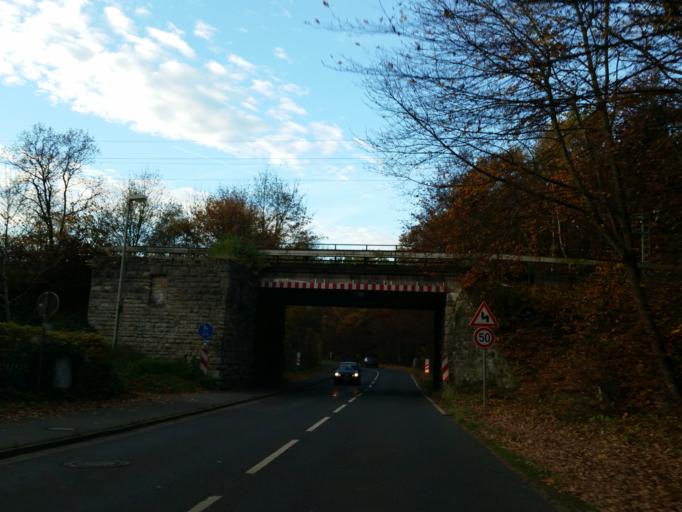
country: DE
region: Lower Saxony
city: Cremlingen
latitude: 52.2601
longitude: 10.5902
